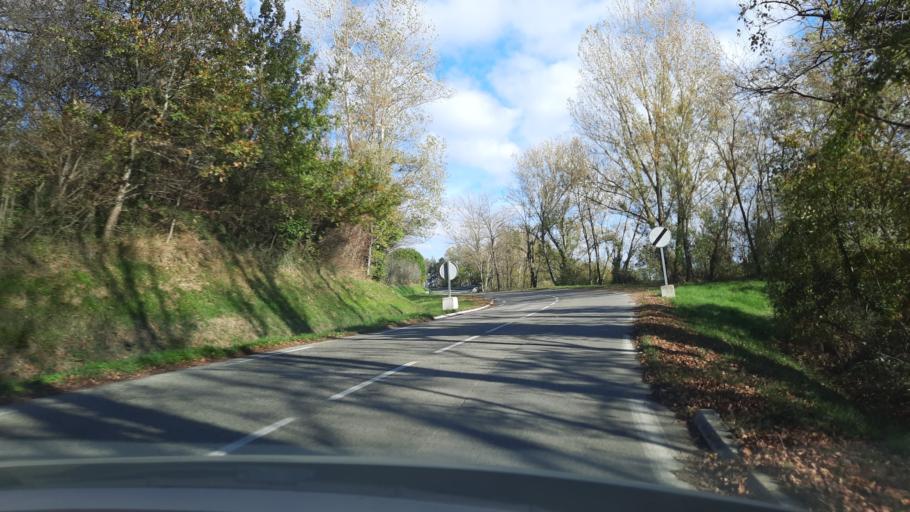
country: FR
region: Midi-Pyrenees
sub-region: Departement du Tarn-et-Garonne
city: Molieres
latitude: 44.1230
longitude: 1.3520
